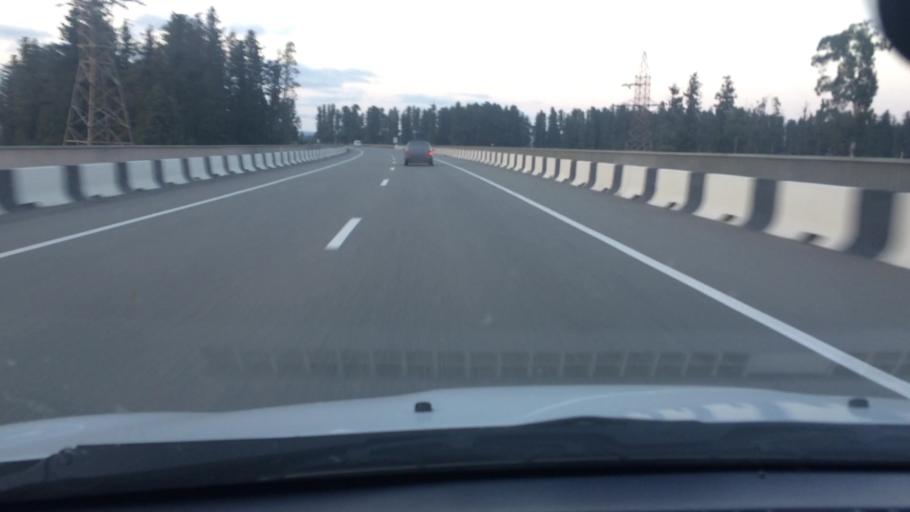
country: GE
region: Ajaria
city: Ochkhamuri
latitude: 41.8527
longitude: 41.8369
